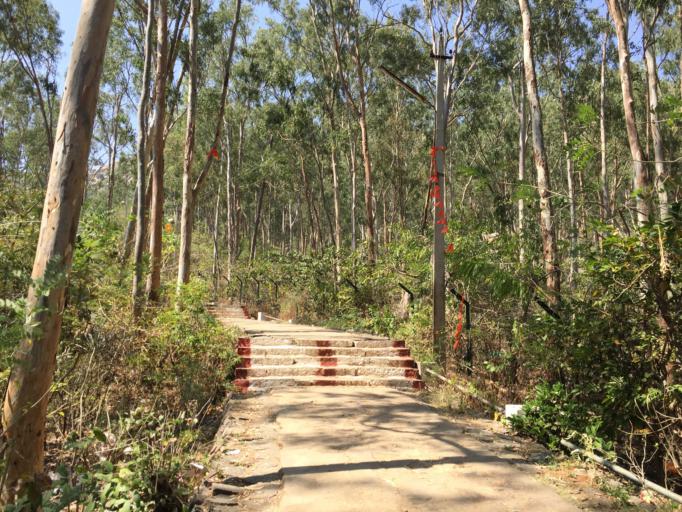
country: IN
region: Karnataka
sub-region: Kolar
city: Kolar
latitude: 13.1418
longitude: 78.1046
